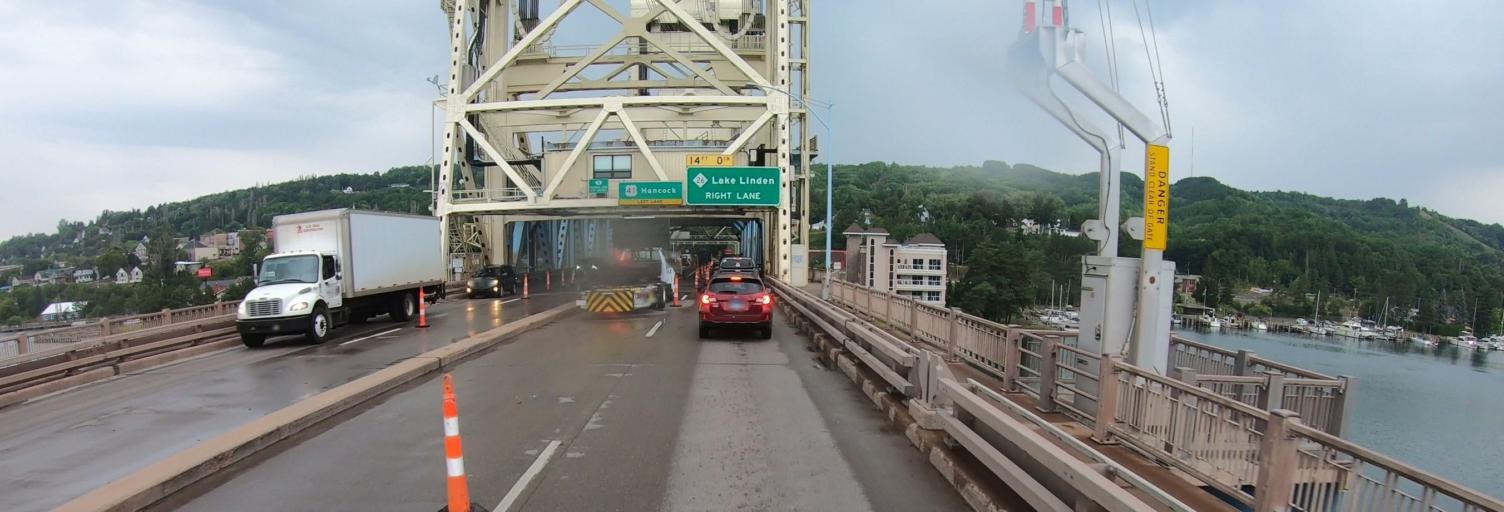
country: US
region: Michigan
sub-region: Houghton County
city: Houghton
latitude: 47.1231
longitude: -88.5738
